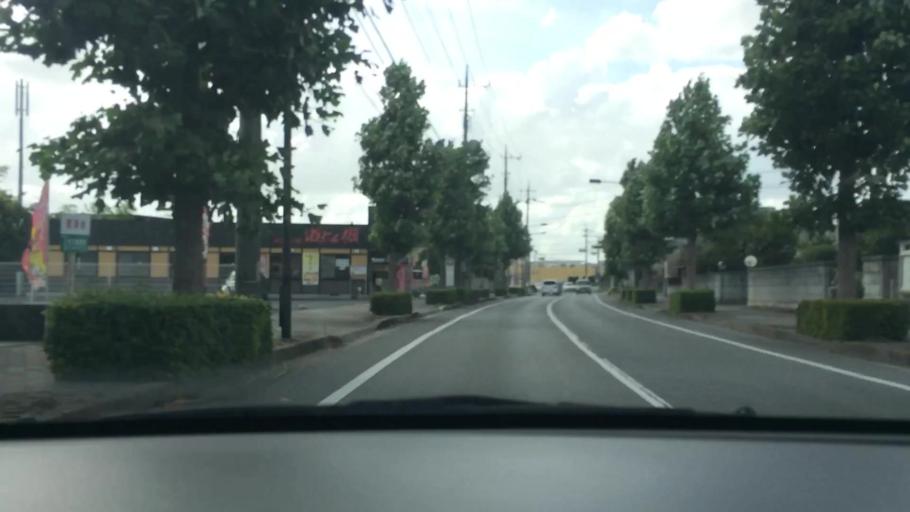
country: JP
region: Chiba
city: Nagareyama
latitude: 35.8993
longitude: 139.9207
